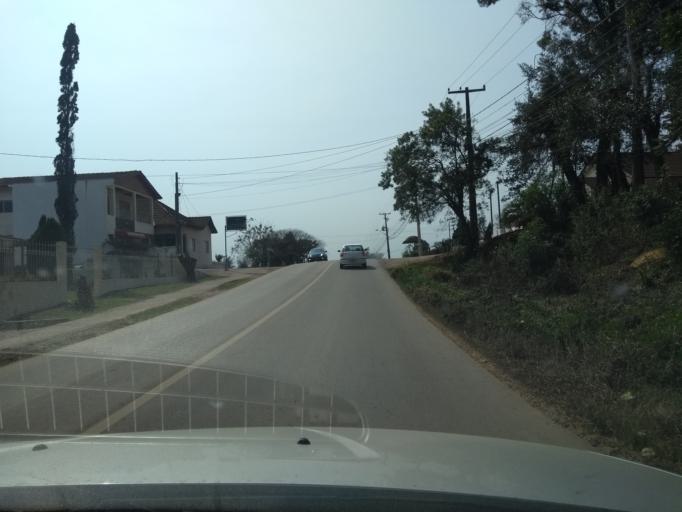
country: BR
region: Parana
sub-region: Araucaria
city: Araucaria
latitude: -25.6150
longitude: -49.3431
